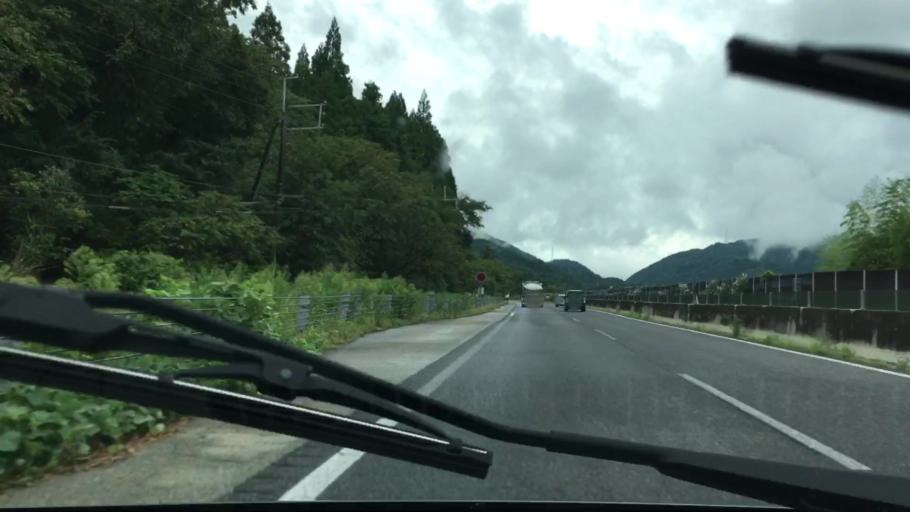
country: JP
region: Hyogo
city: Yamazakicho-nakabirose
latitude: 35.0190
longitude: 134.5034
